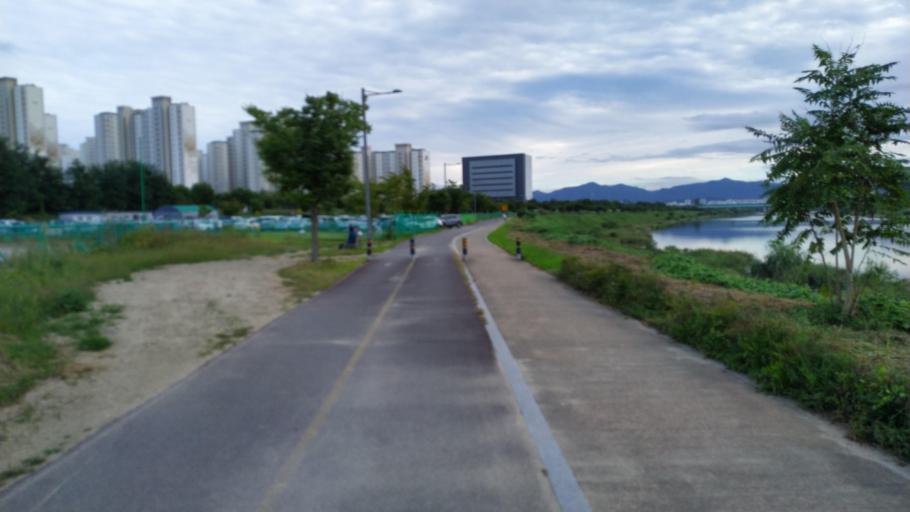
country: KR
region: Daegu
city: Daegu
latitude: 35.9282
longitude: 128.6312
